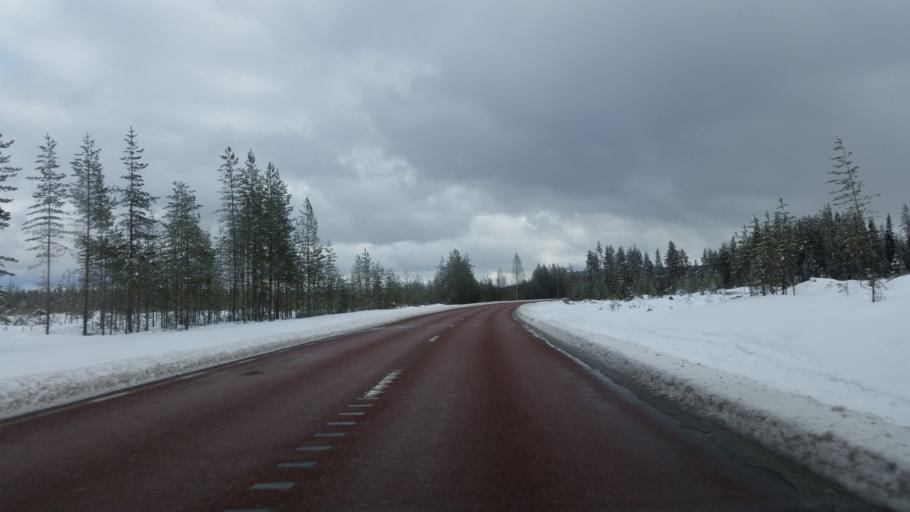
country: SE
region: Gaevleborg
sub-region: Ljusdals Kommun
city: Farila
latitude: 61.9002
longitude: 15.6457
